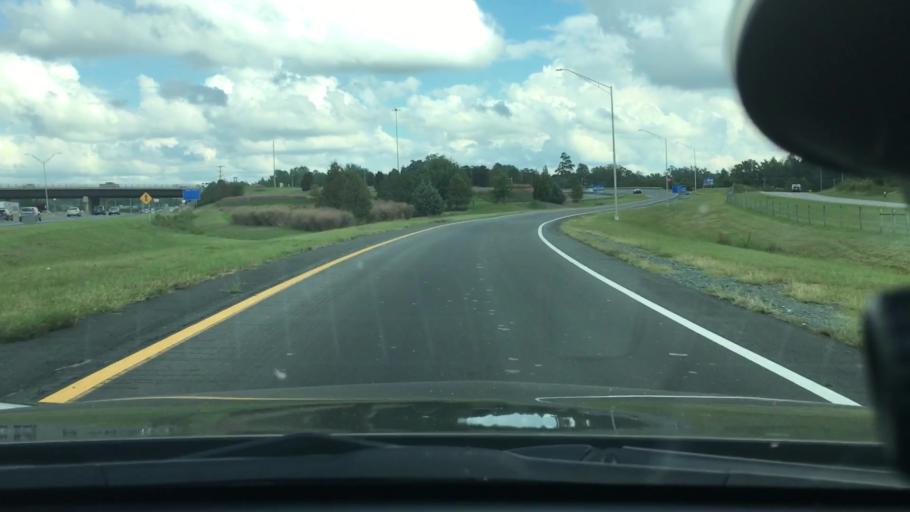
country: US
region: North Carolina
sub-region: Alamance County
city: Elon
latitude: 36.0646
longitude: -79.5191
